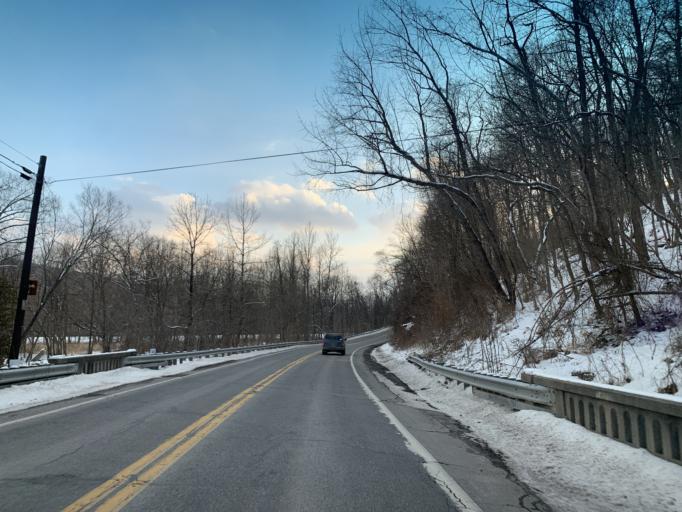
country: US
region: Maryland
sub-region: Allegany County
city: Cumberland
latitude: 39.7395
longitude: -78.7598
